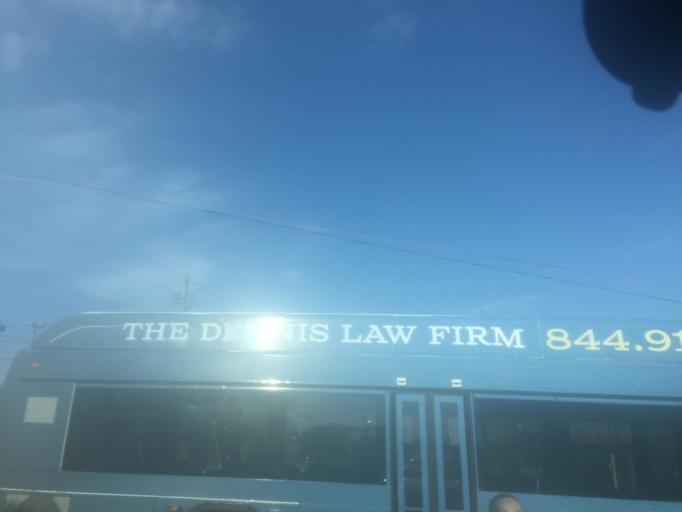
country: US
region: Georgia
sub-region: Clayton County
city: Riverdale
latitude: 33.5611
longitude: -84.4145
